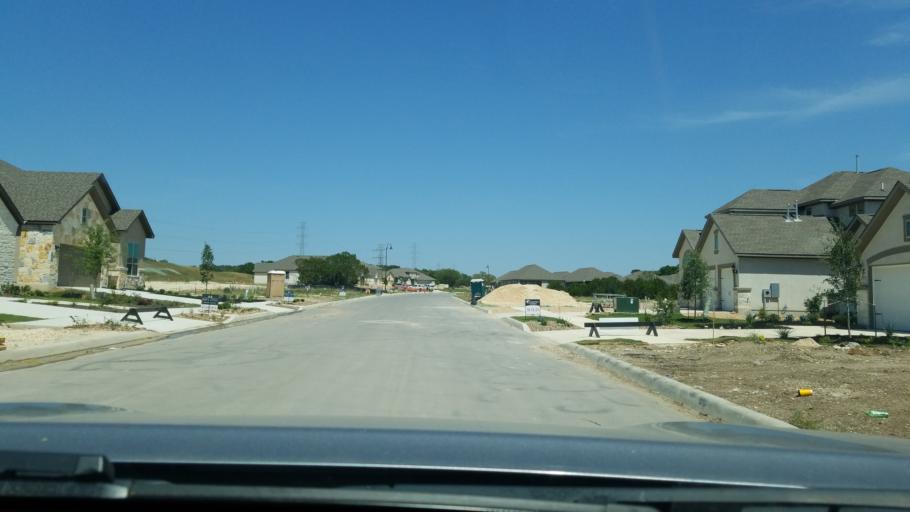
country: US
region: Texas
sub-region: Kendall County
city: Boerne
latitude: 29.8033
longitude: -98.6966
